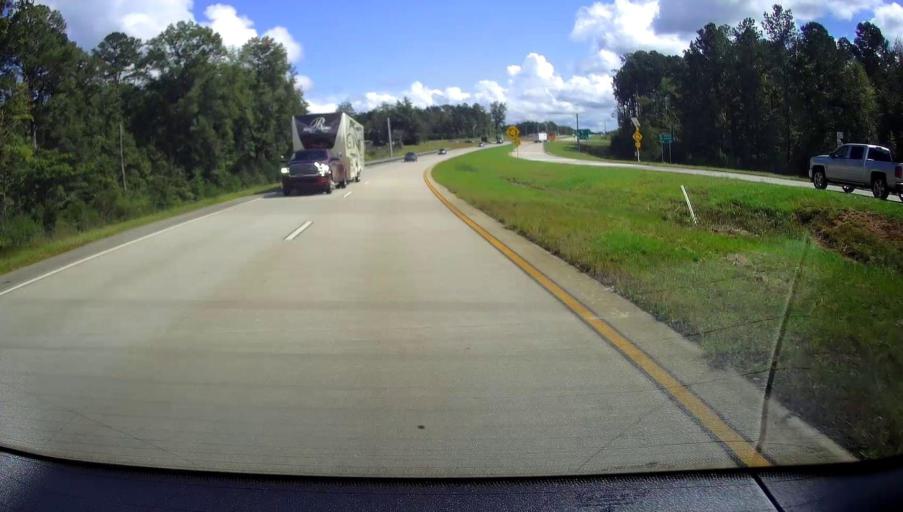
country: US
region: Georgia
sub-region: Jones County
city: Gray
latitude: 33.0291
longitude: -83.5242
